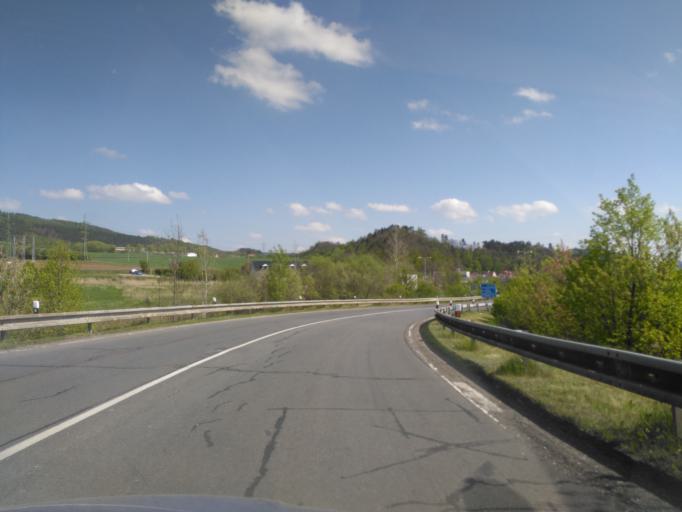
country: CZ
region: Central Bohemia
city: Zdice
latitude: 49.9022
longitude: 13.9596
